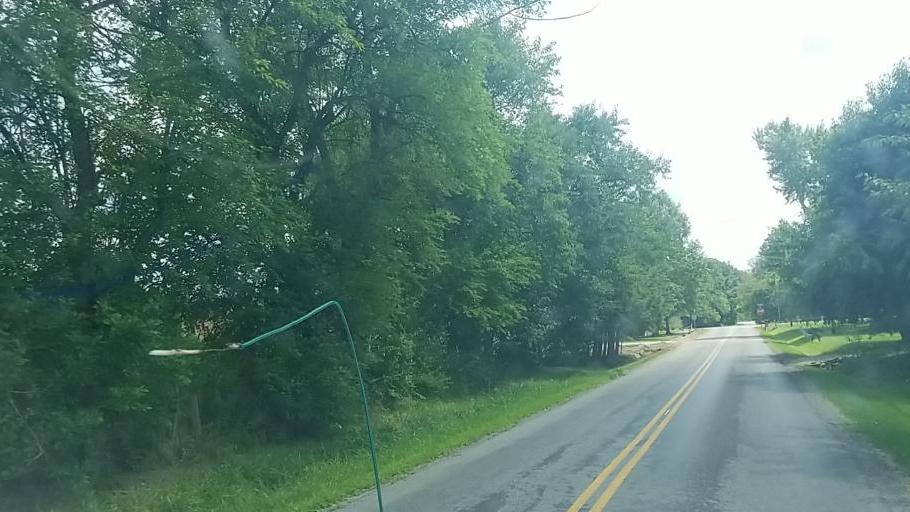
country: US
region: Ohio
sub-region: Medina County
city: Lodi
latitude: 41.0140
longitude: -82.0561
